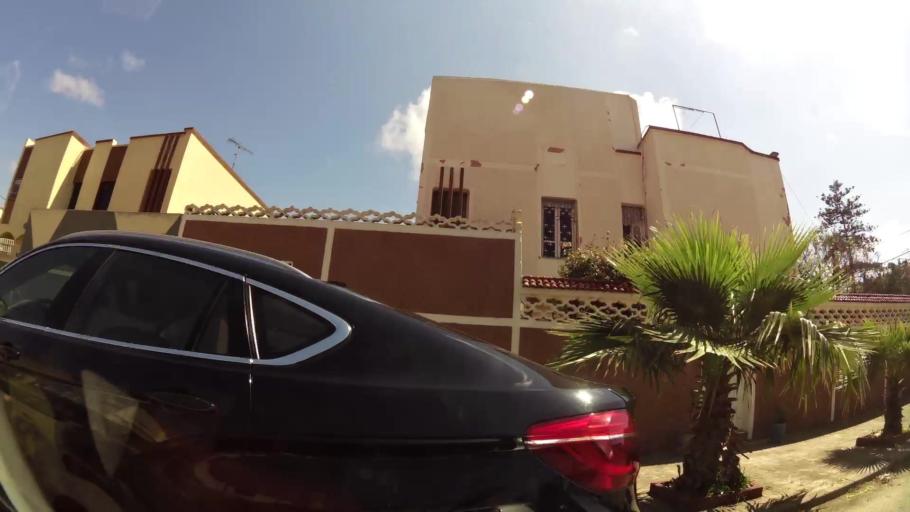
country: MA
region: Rabat-Sale-Zemmour-Zaer
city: Sale
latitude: 34.0421
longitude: -6.7860
